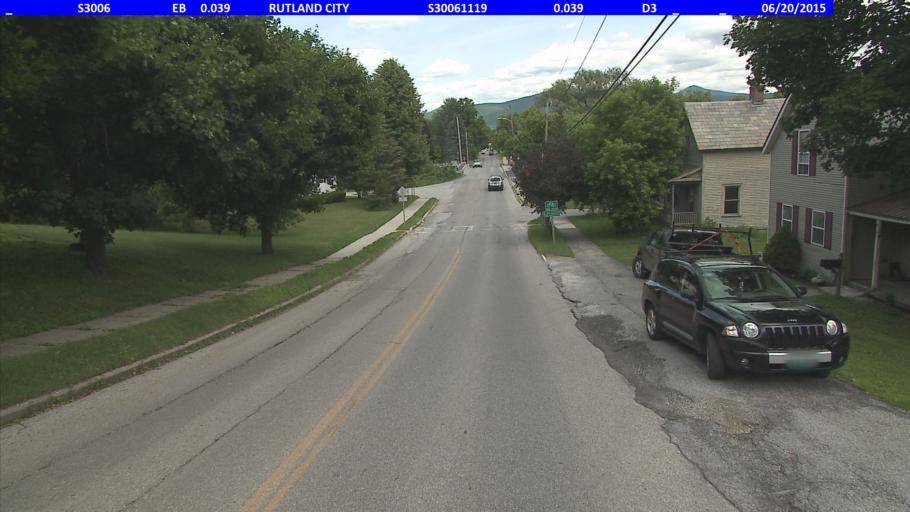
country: US
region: Vermont
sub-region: Rutland County
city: Rutland
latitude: 43.6142
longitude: -72.9911
